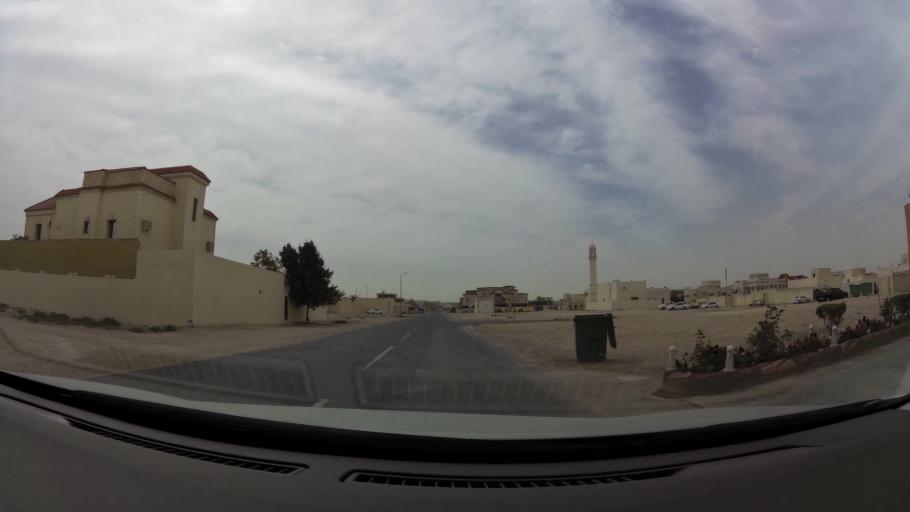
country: QA
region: Baladiyat ad Dawhah
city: Doha
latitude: 25.2136
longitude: 51.4728
